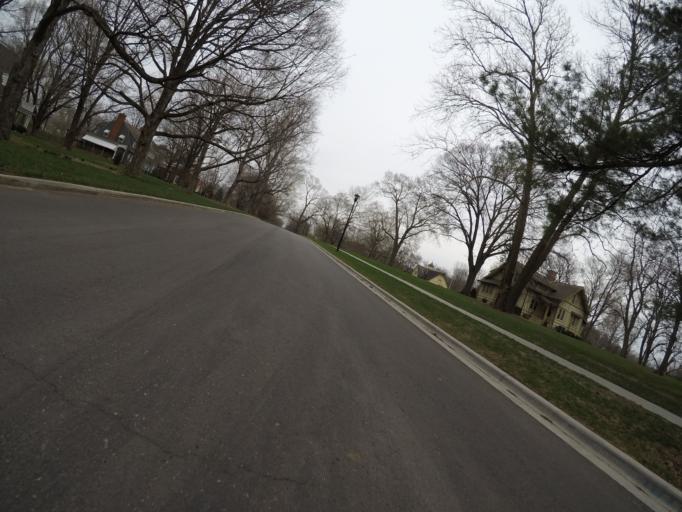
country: US
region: Kansas
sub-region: Johnson County
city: Olathe
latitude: 38.8792
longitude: -94.8113
